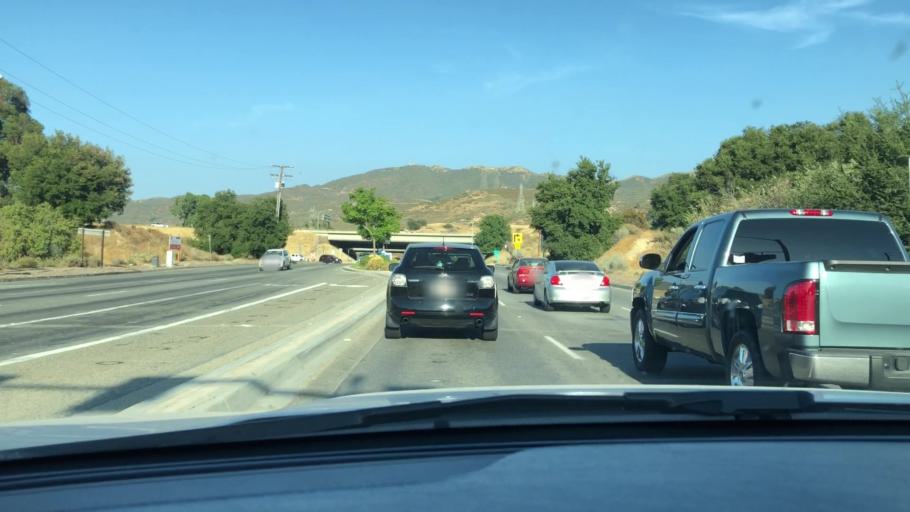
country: US
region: California
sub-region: Los Angeles County
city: Santa Clarita
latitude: 34.3657
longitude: -118.5060
